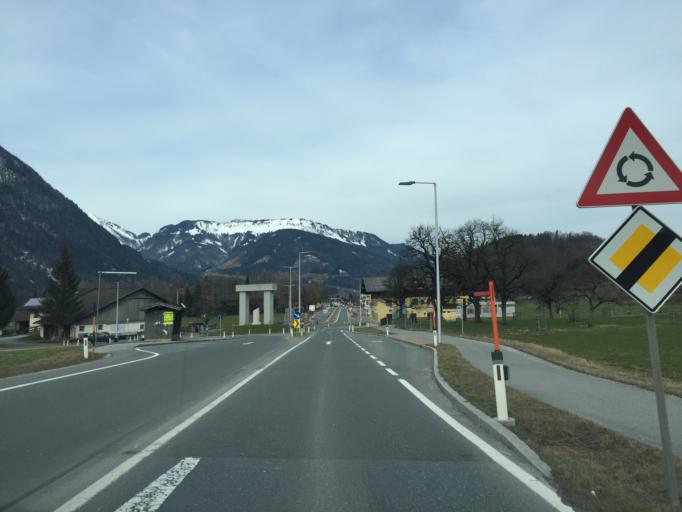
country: AT
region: Salzburg
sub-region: Politischer Bezirk Hallein
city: Golling an der Salzach
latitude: 47.5906
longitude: 13.1777
